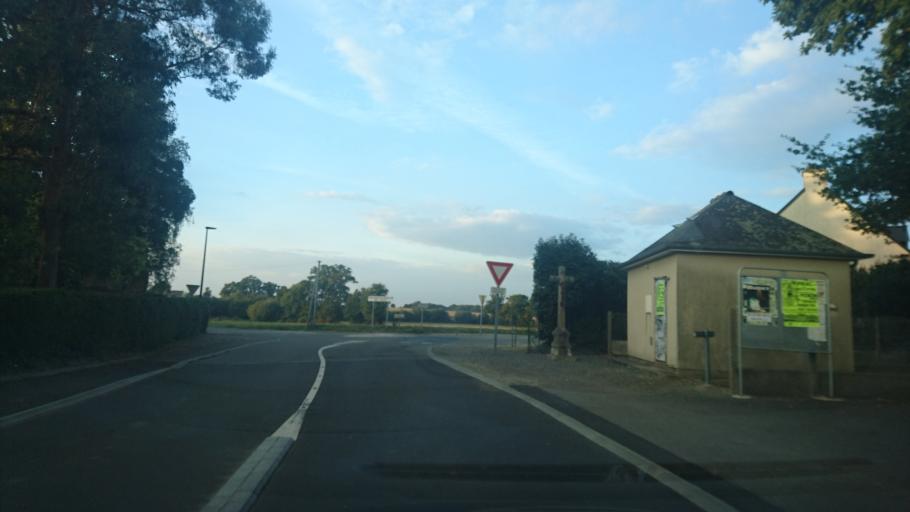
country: FR
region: Brittany
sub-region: Departement d'Ille-et-Vilaine
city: Pipriac
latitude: 47.8526
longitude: -1.9437
